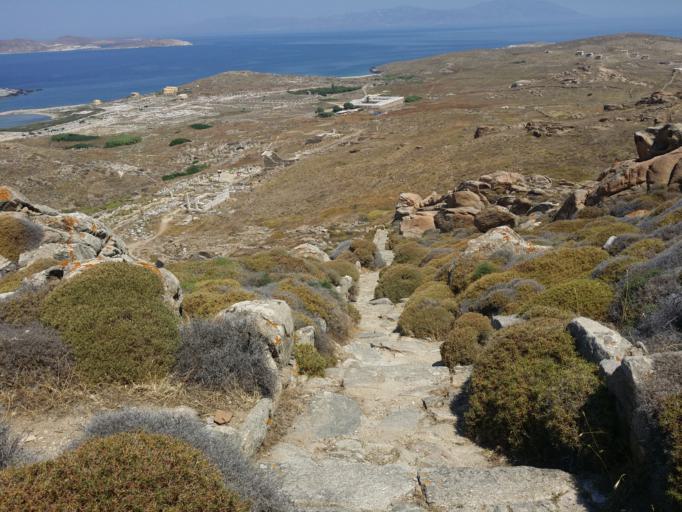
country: GR
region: South Aegean
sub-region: Nomos Kykladon
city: Mykonos
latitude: 37.3959
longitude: 25.2720
